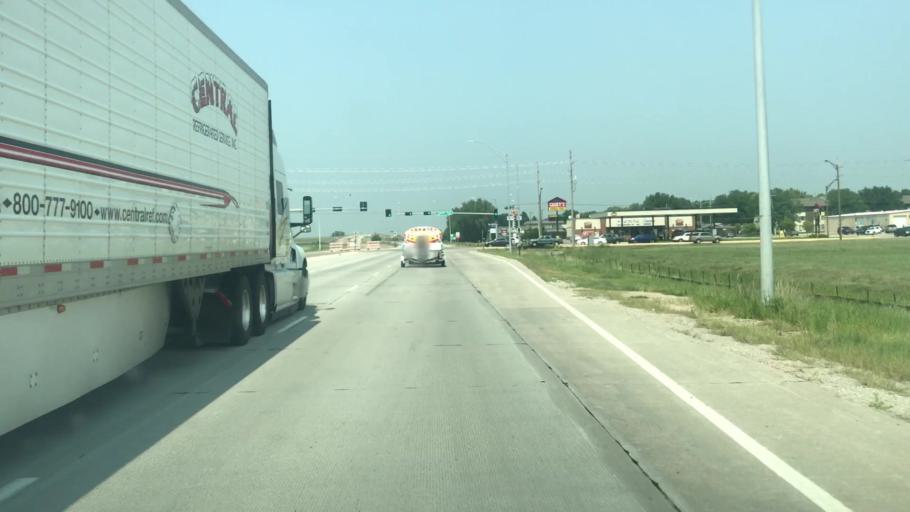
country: US
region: Nebraska
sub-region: Hall County
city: Grand Island
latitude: 40.9447
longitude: -98.3835
